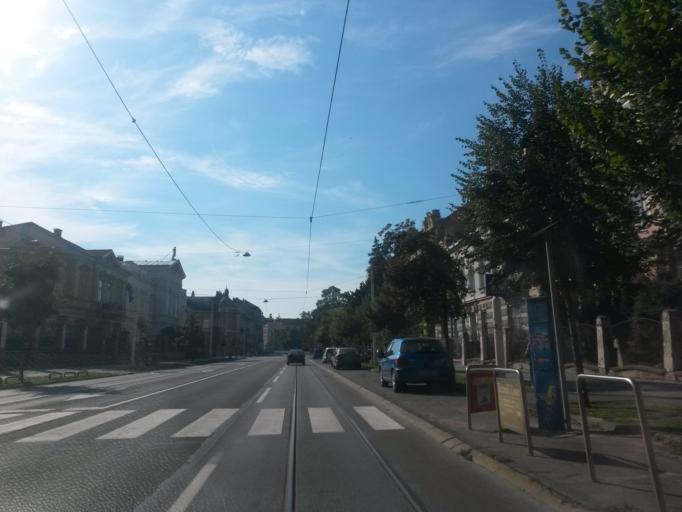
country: HR
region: Osjecko-Baranjska
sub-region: Grad Osijek
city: Osijek
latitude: 45.5607
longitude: 18.6842
